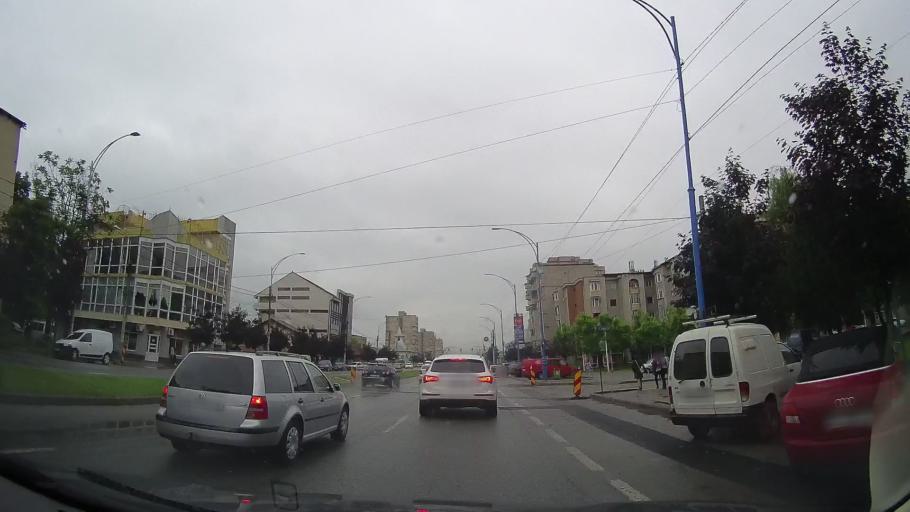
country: RO
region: Mehedinti
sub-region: Municipiul Drobeta-Turnu Severin
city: Drobeta-Turnu Severin
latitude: 44.6325
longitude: 22.6707
